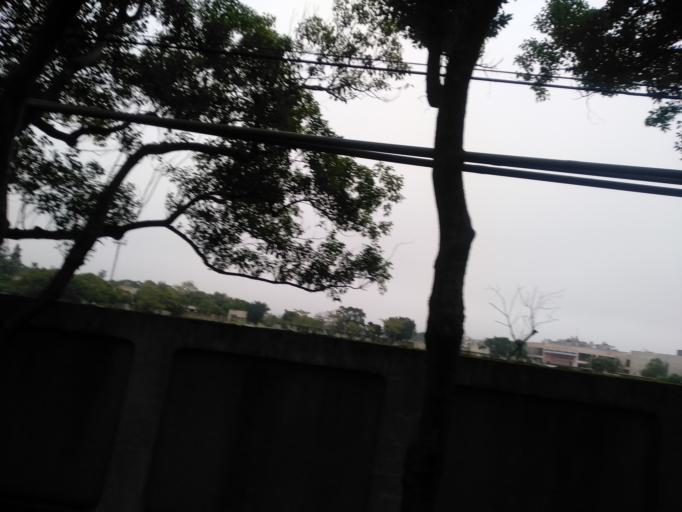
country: TW
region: Taiwan
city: Taoyuan City
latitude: 24.9984
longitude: 121.1619
